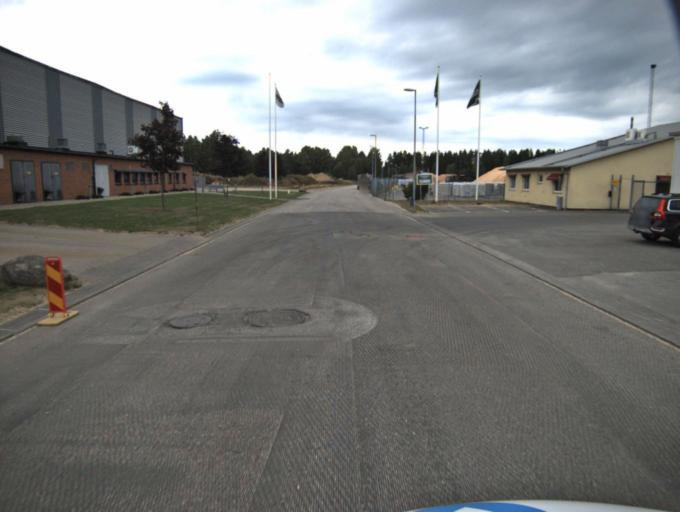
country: SE
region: Vaestra Goetaland
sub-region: Ulricehamns Kommun
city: Ulricehamn
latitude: 57.8269
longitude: 13.4206
